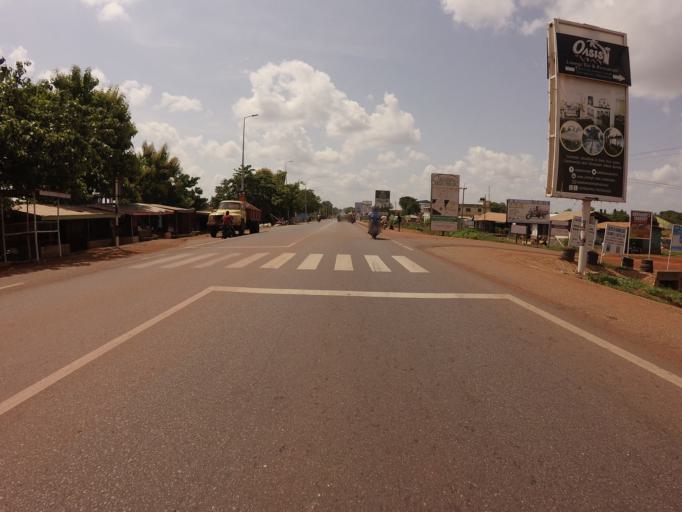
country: GH
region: Northern
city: Tamale
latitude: 9.4416
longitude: -0.8439
